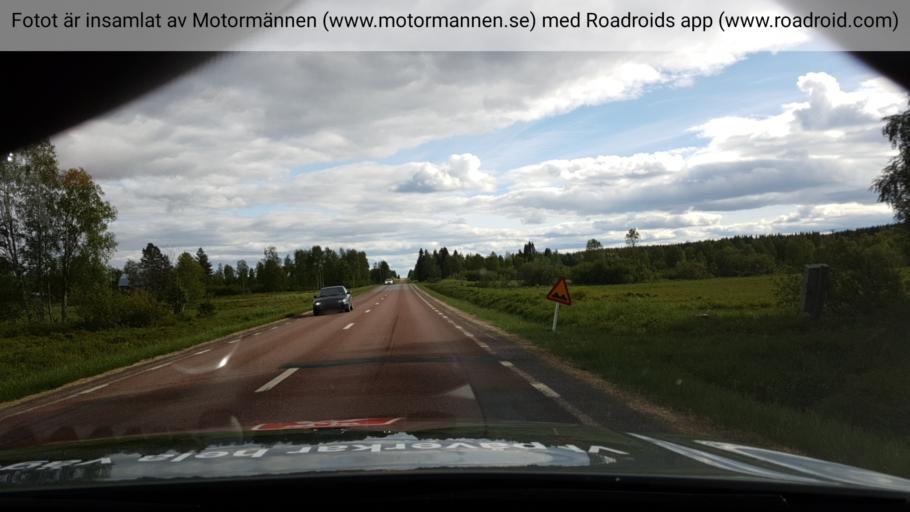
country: SE
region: Jaemtland
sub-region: Stroemsunds Kommun
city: Stroemsund
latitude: 63.7876
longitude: 15.5114
